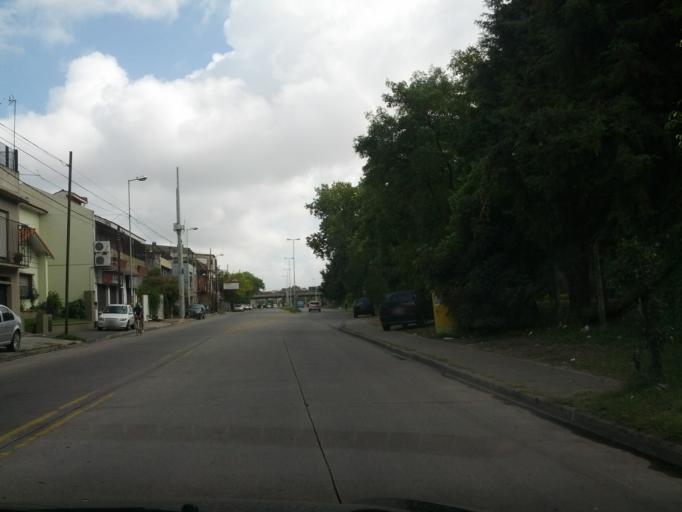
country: AR
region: Buenos Aires
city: Caseros
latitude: -34.6323
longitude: -58.5590
